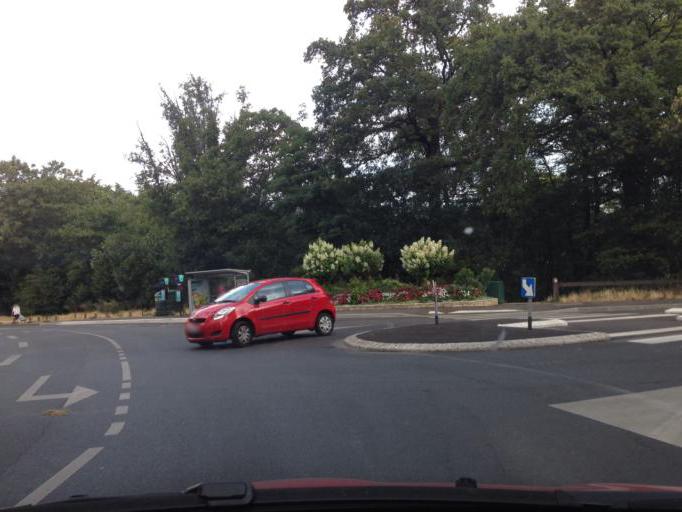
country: FR
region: Ile-de-France
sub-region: Departement des Hauts-de-Seine
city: Meudon
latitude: 48.7888
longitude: 2.2345
